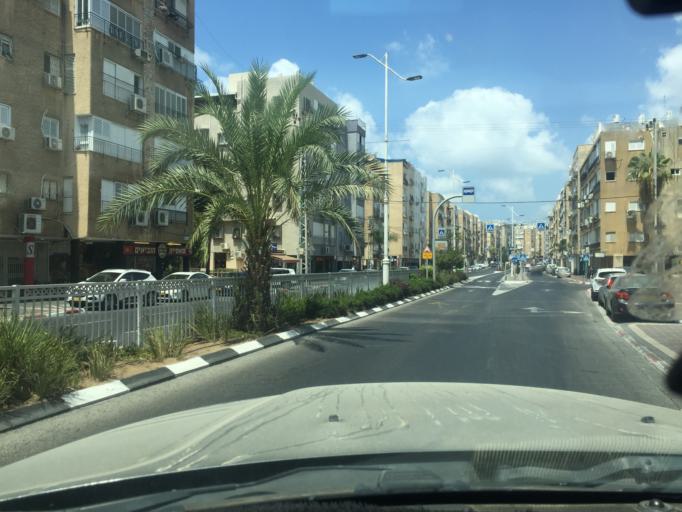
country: IL
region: Tel Aviv
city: Bat Yam
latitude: 32.0113
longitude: 34.7420
